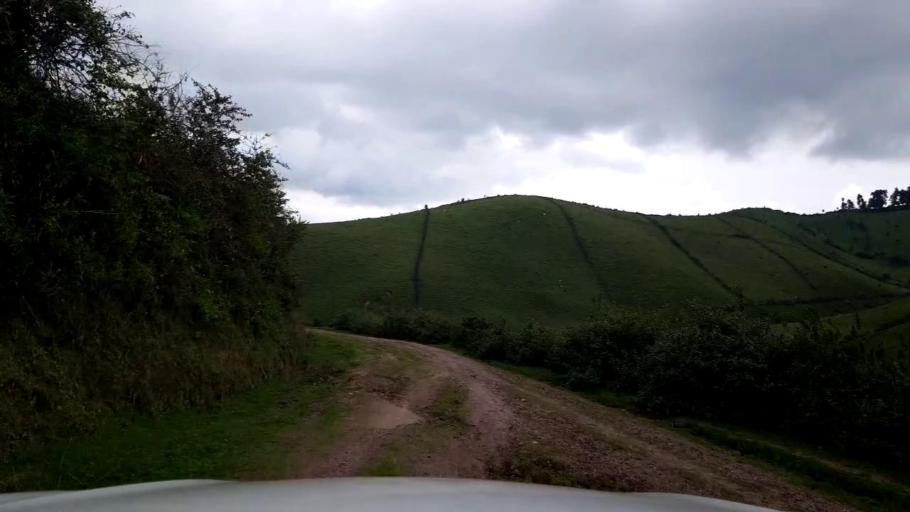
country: RW
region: Western Province
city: Gisenyi
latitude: -1.6802
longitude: 29.4181
